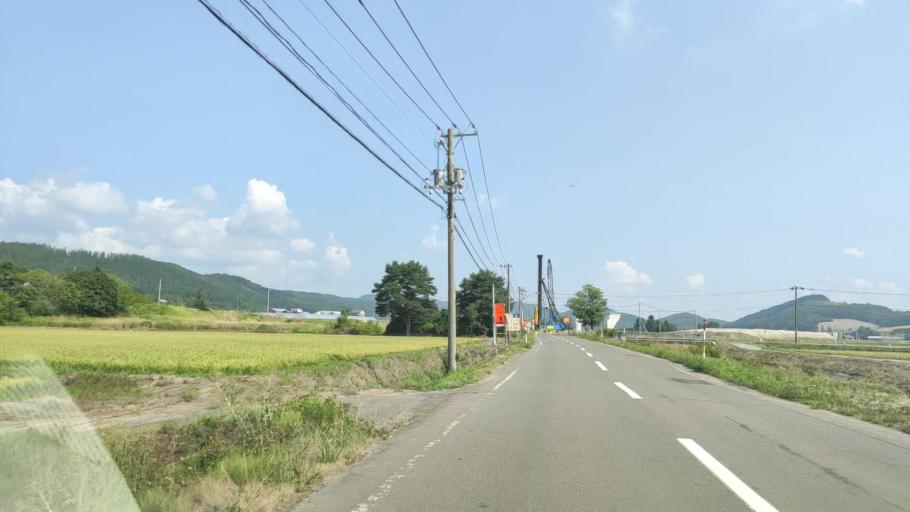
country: JP
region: Hokkaido
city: Shimo-furano
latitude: 43.3853
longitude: 142.3929
